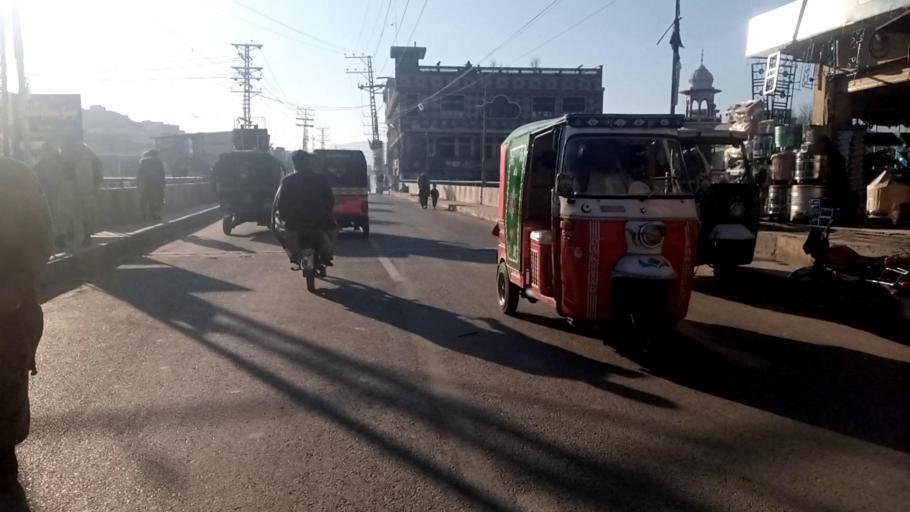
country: PK
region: Khyber Pakhtunkhwa
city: Mingora
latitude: 34.7723
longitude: 72.3556
